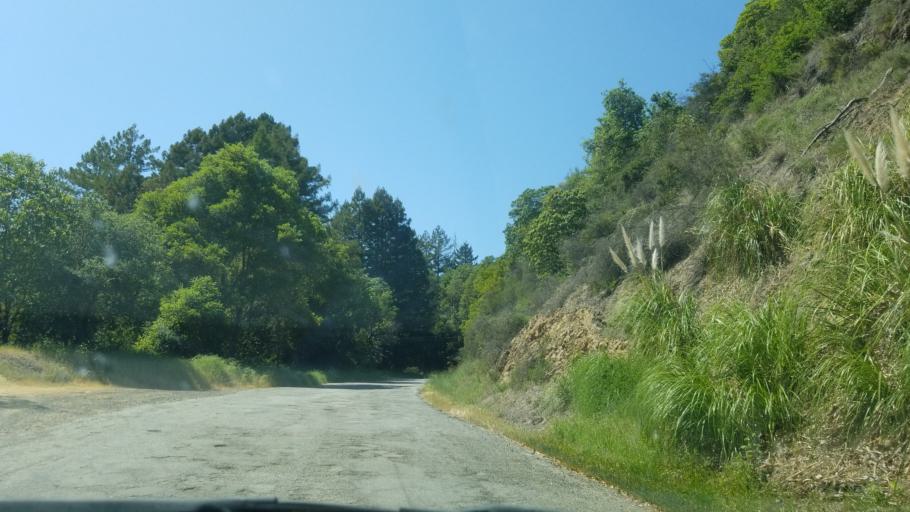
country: US
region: California
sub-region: Santa Cruz County
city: Day Valley
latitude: 37.0650
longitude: -121.8318
